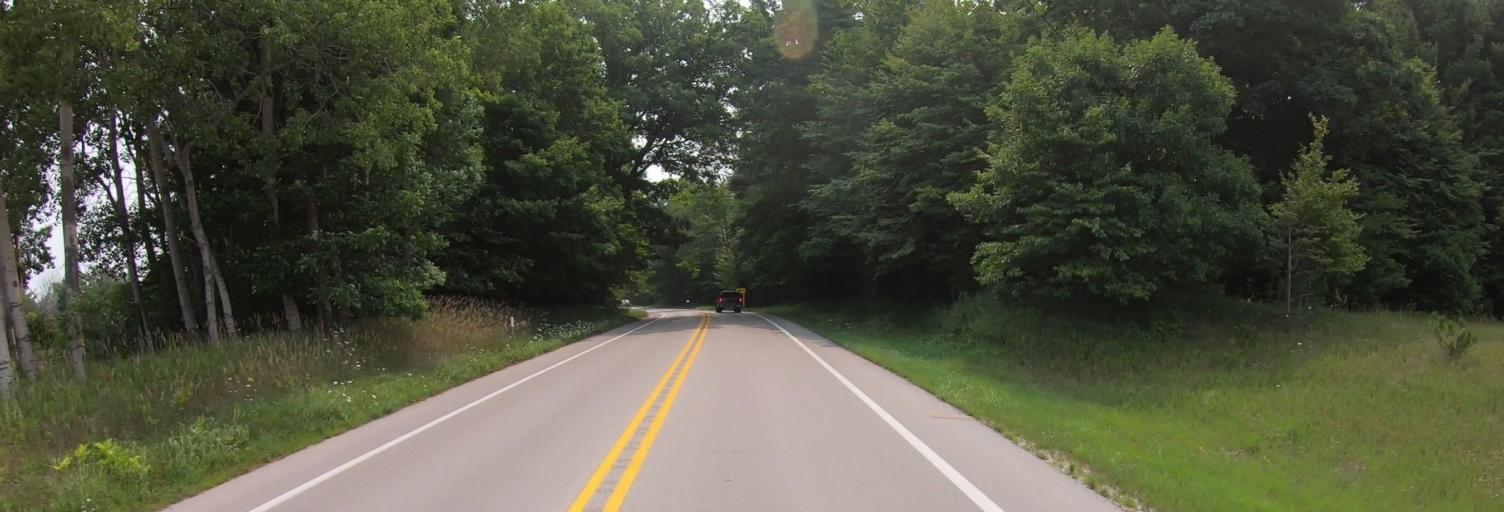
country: US
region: Michigan
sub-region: Leelanau County
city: Leland
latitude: 44.9361
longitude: -85.9261
